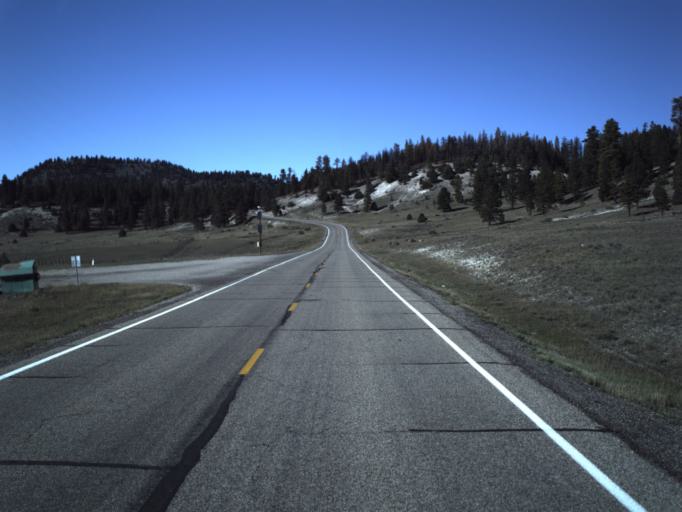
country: US
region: Utah
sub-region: Iron County
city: Parowan
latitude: 37.6845
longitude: -112.6649
